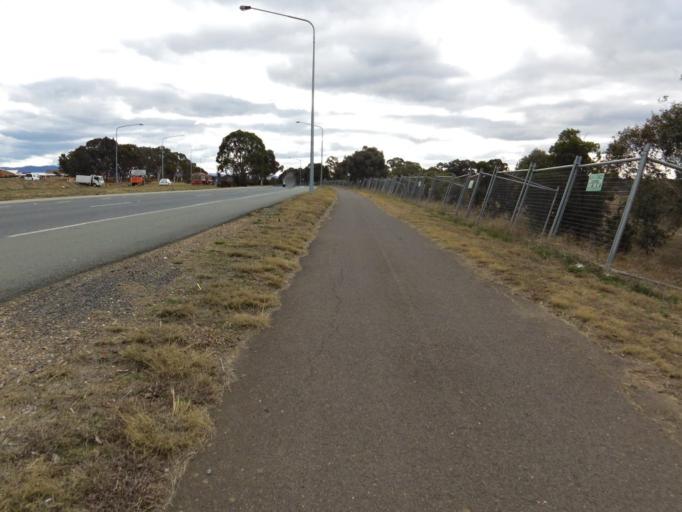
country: AU
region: Australian Capital Territory
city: Belconnen
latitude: -35.2321
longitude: 149.0851
